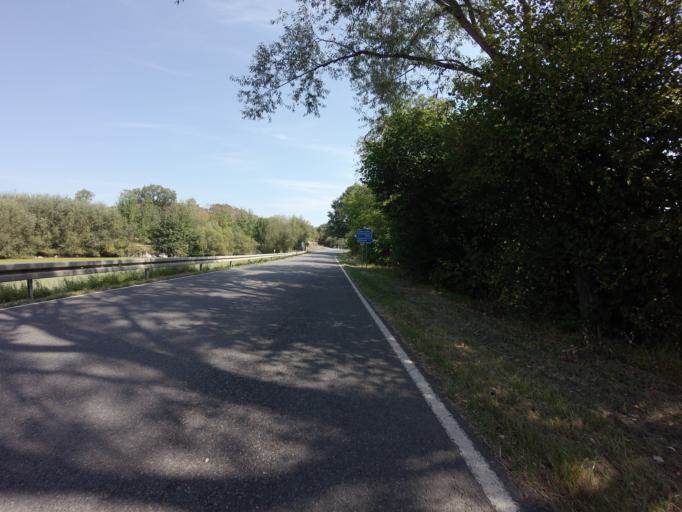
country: CZ
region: Central Bohemia
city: Sedlcany
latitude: 49.6119
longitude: 14.3852
